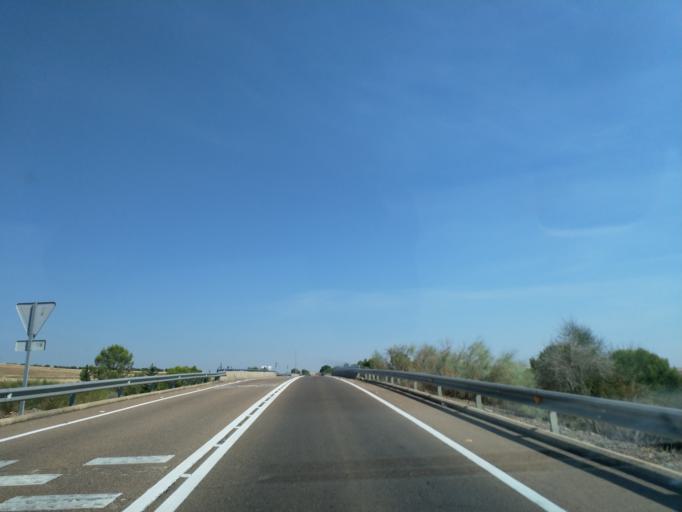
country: ES
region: Extremadura
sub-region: Provincia de Badajoz
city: Merida
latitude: 38.9415
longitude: -6.3429
